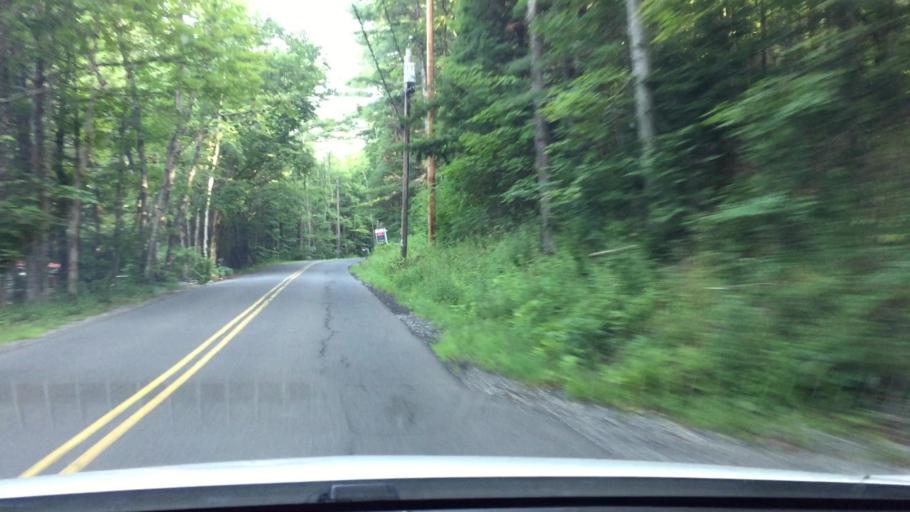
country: US
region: Massachusetts
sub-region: Berkshire County
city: Otis
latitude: 42.2387
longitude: -73.1132
